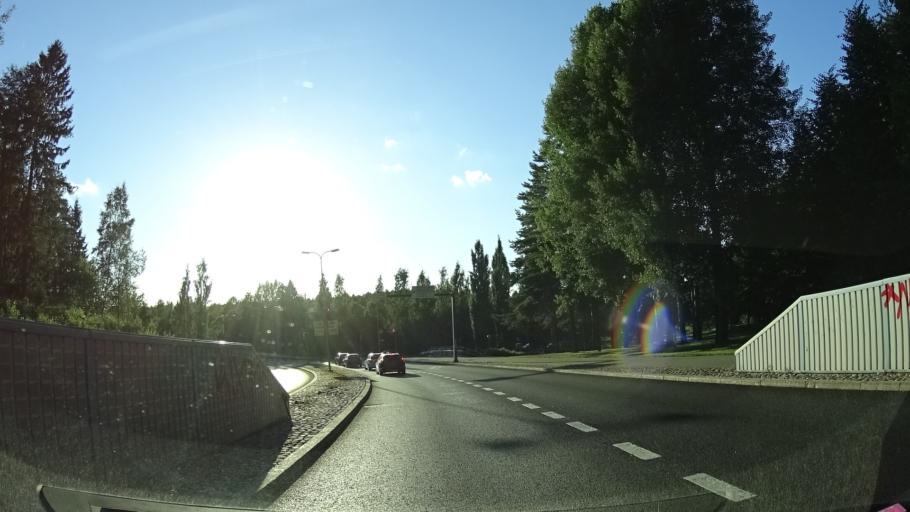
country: FI
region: Uusimaa
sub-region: Helsinki
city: Teekkarikylae
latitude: 60.2647
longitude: 24.8662
